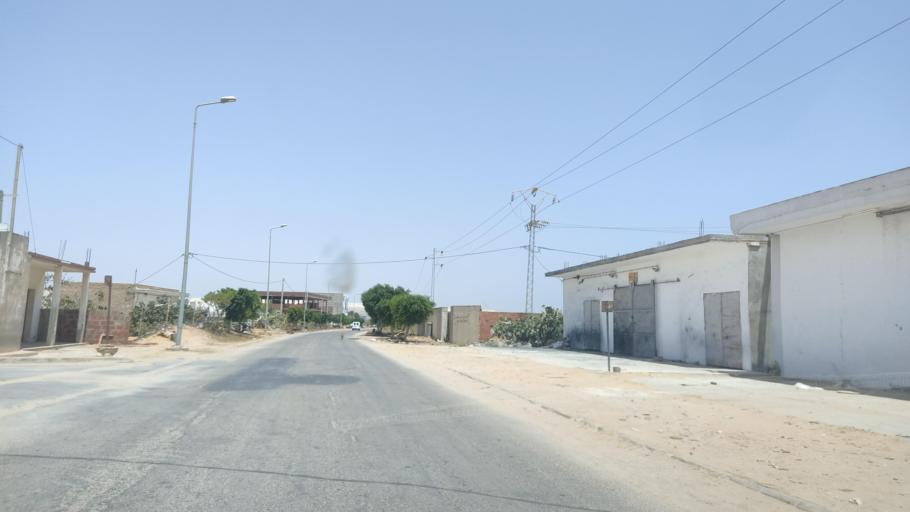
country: TN
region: Safaqis
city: Sfax
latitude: 34.6825
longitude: 10.7215
